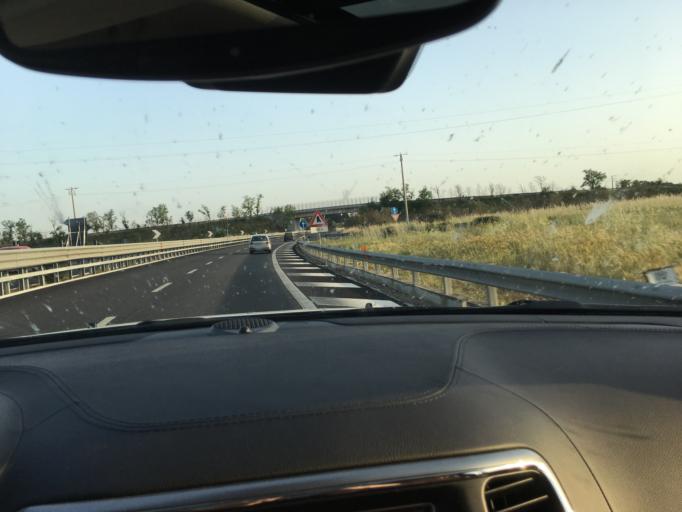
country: IT
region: Apulia
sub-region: Provincia di Lecce
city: Lequile
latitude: 40.2912
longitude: 18.1330
